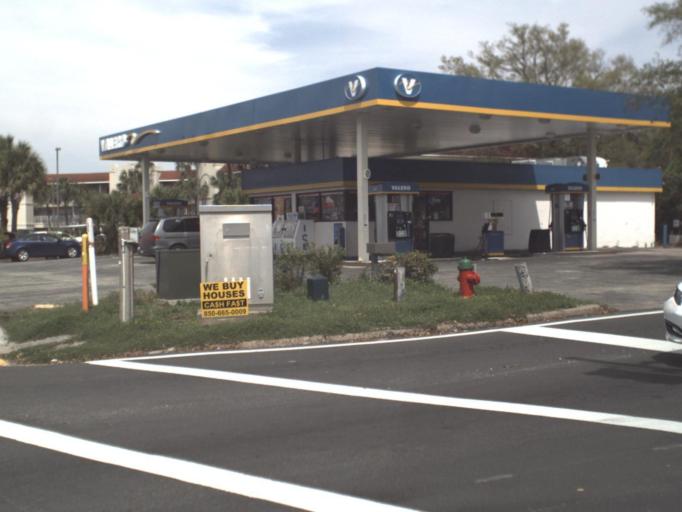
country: US
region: Florida
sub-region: Okaloosa County
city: Ocean City
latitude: 30.4237
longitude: -86.6093
